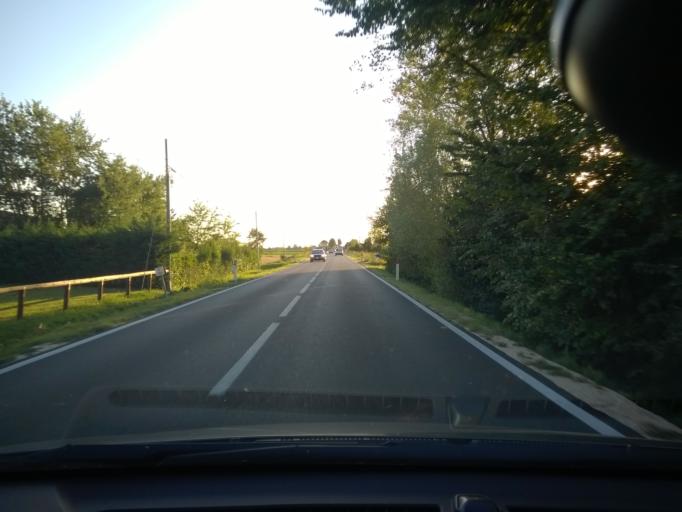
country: IT
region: Veneto
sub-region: Provincia di Venezia
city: Annone Veneto
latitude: 45.7901
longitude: 12.6620
